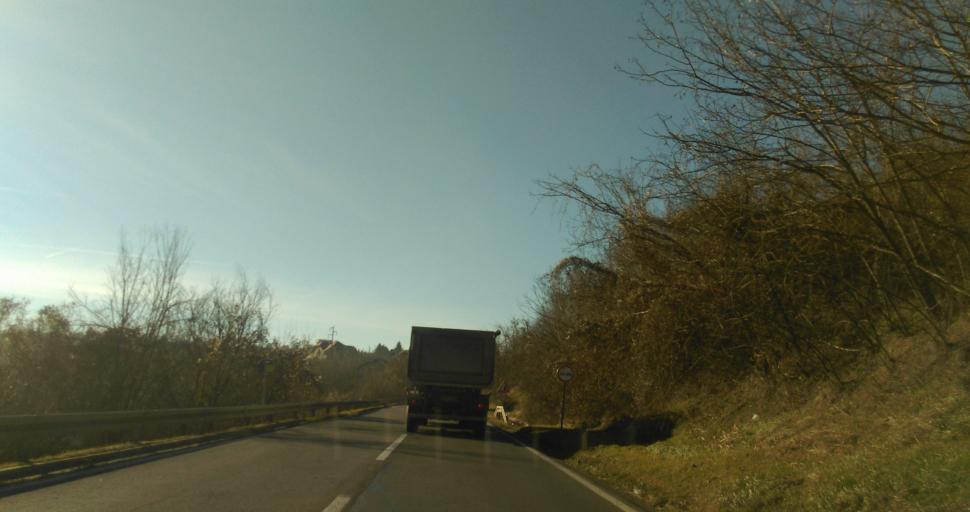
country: RS
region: Autonomna Pokrajina Vojvodina
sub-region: Juznobacki Okrug
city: Petrovaradin
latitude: 45.2144
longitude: 19.8545
